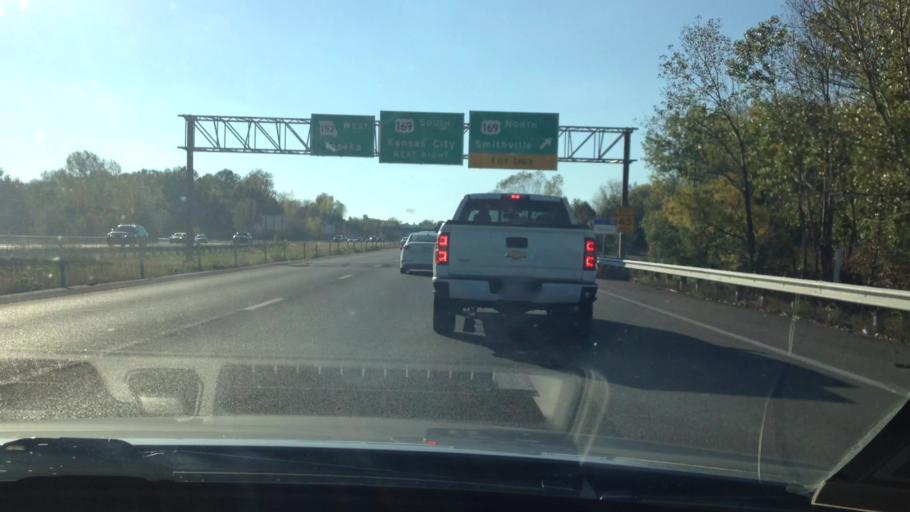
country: US
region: Missouri
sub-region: Clay County
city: Gladstone
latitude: 39.2606
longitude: -94.5806
